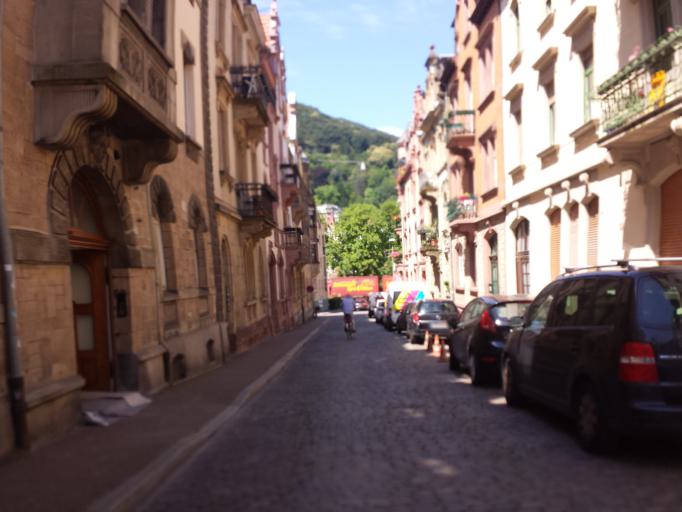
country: DE
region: Baden-Wuerttemberg
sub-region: Karlsruhe Region
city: Heidelberg
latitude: 49.4128
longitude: 8.7118
